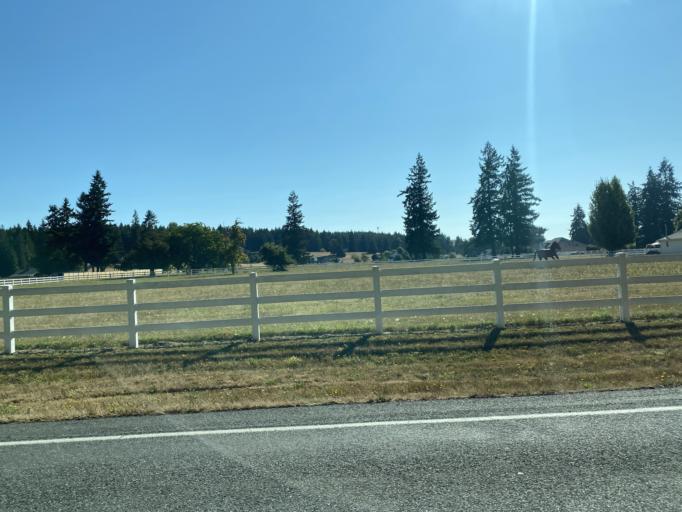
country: US
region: Washington
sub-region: Thurston County
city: Tanglewilde-Thompson Place
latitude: 46.9685
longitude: -122.7646
